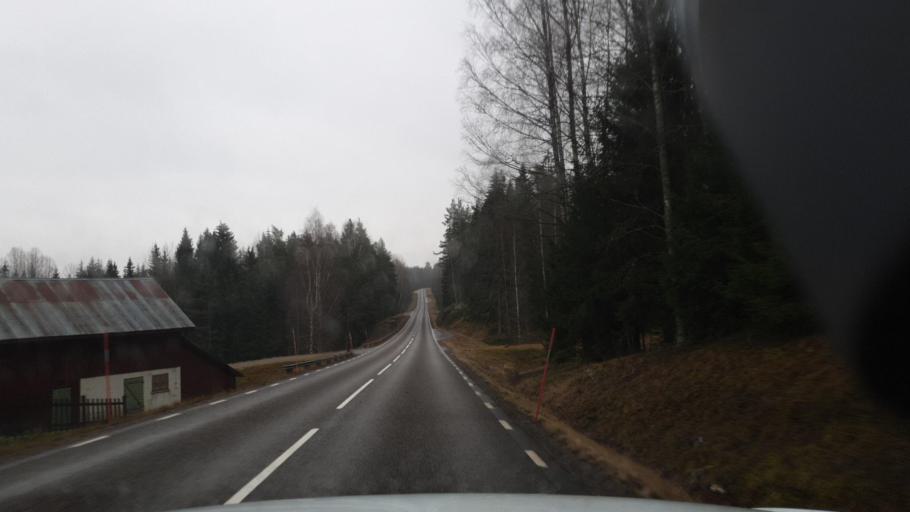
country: SE
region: Vaermland
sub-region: Eda Kommun
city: Amotfors
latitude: 59.7357
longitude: 12.4075
